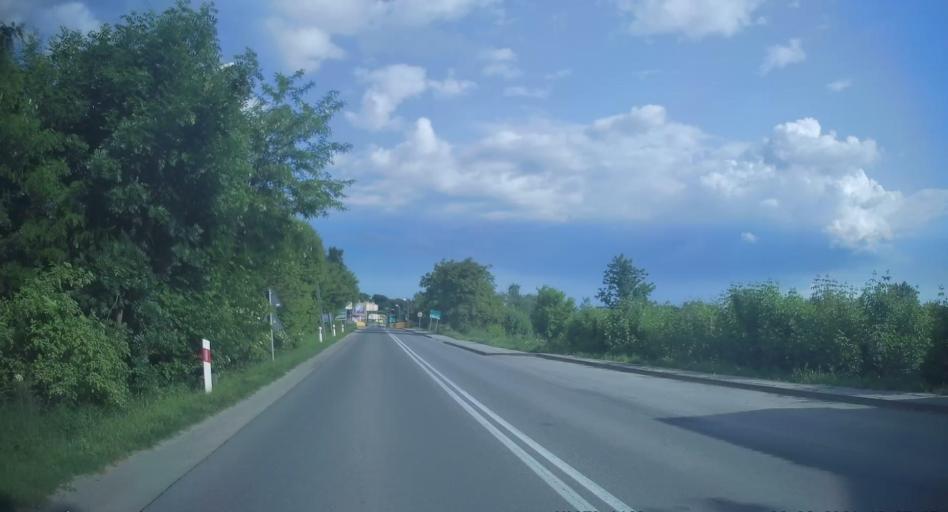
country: PL
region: Subcarpathian Voivodeship
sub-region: Powiat debicki
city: Debica
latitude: 50.0657
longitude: 21.4018
